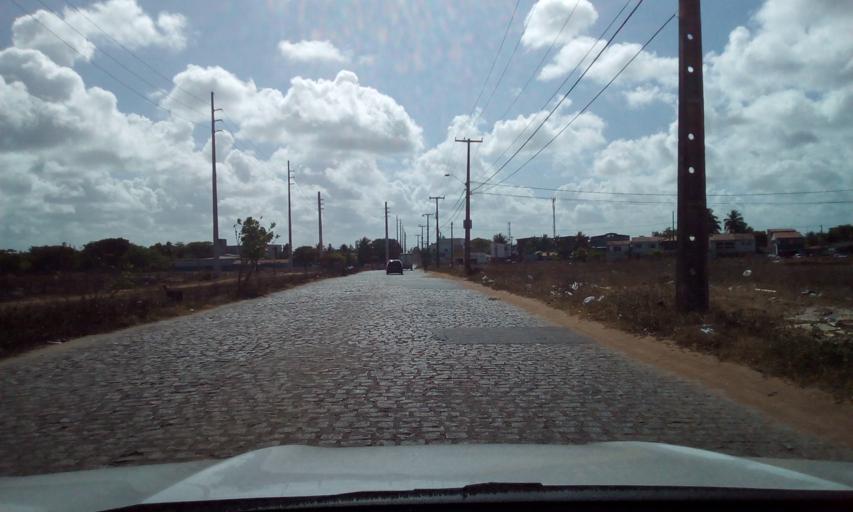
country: BR
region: Paraiba
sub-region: Joao Pessoa
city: Joao Pessoa
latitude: -7.0776
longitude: -34.8445
